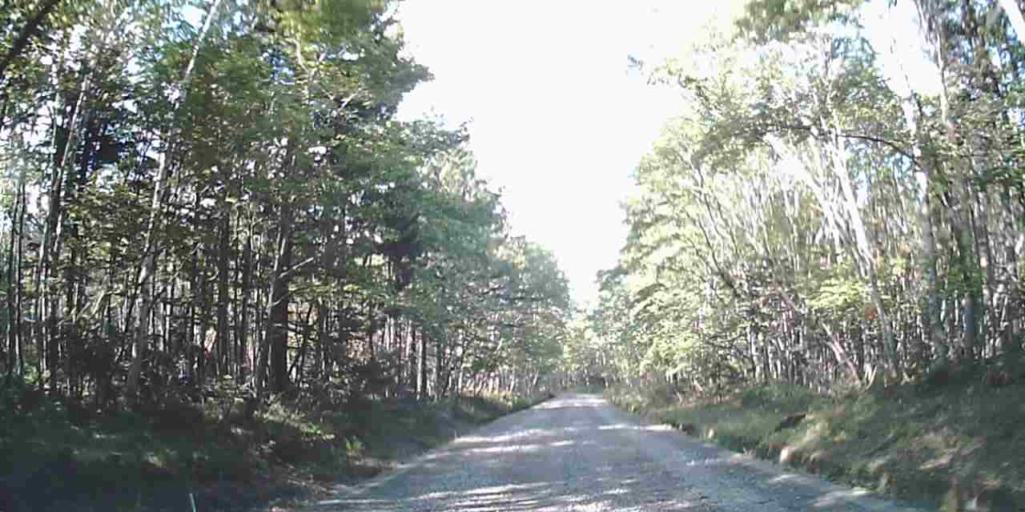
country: JP
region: Hokkaido
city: Shiraoi
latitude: 42.7097
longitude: 141.3988
